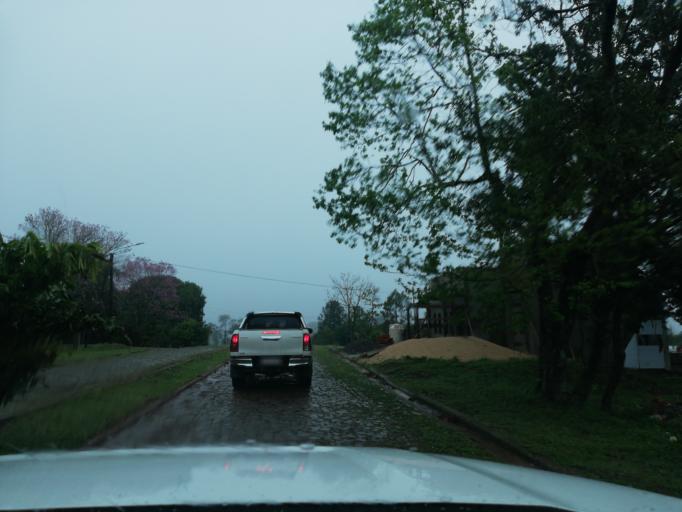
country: AR
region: Misiones
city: Almafuerte
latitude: -27.5076
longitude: -55.4039
